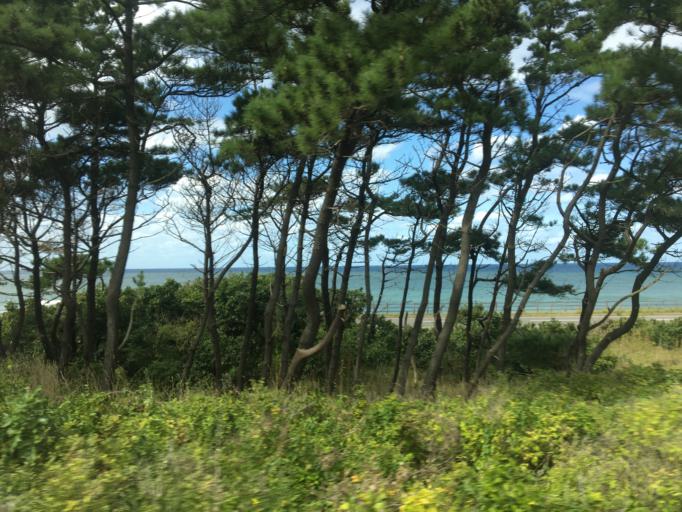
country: JP
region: Aomori
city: Shimokizukuri
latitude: 40.7651
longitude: 140.1655
